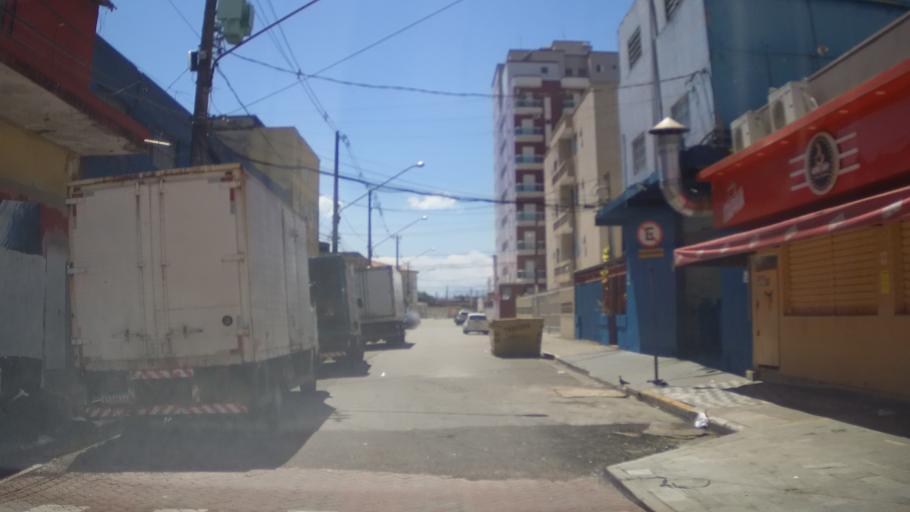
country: BR
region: Sao Paulo
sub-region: Praia Grande
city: Praia Grande
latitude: -24.0265
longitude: -46.4766
